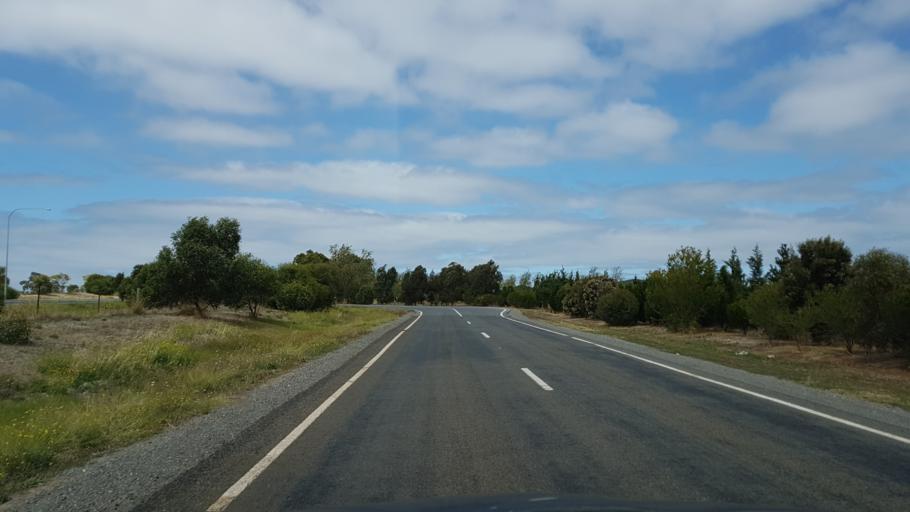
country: AU
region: South Australia
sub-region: Onkaparinga
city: McLaren Vale
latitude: -35.2114
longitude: 138.5231
